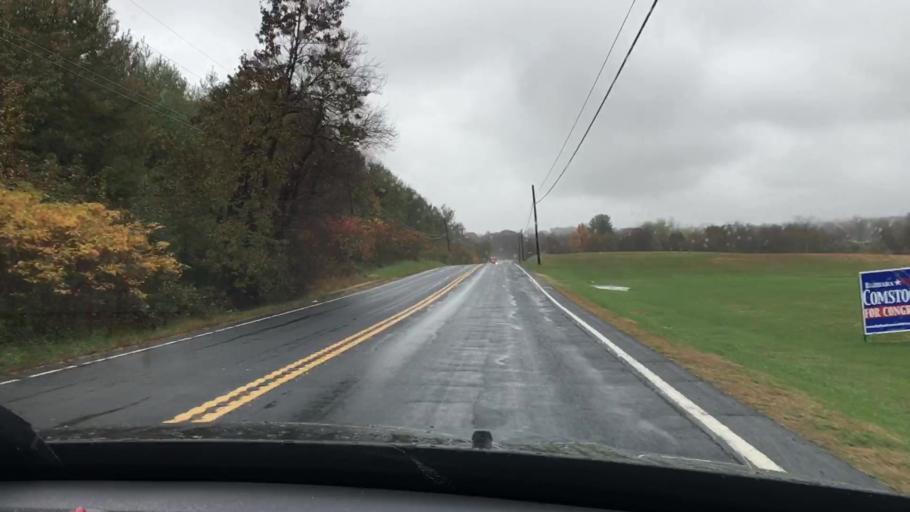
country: US
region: Maryland
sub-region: Frederick County
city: Point of Rocks
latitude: 39.2408
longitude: -77.5317
